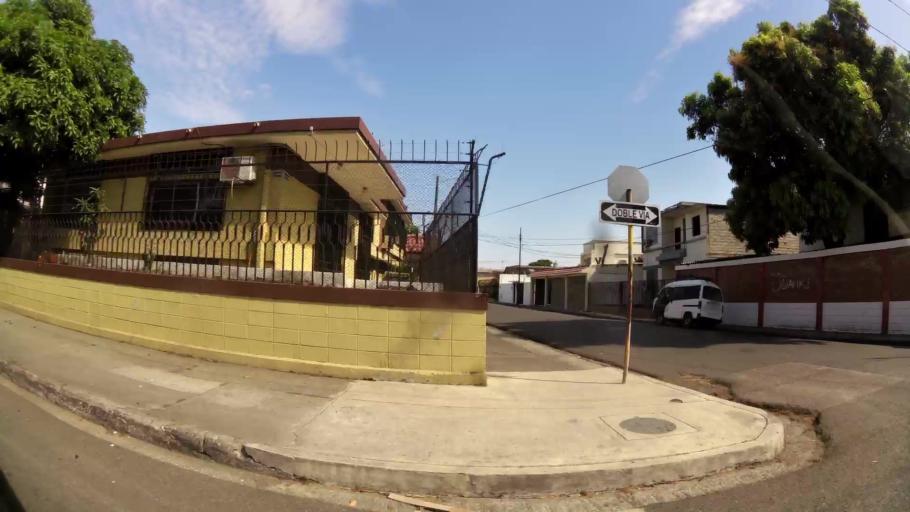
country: EC
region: Guayas
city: Guayaquil
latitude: -2.2203
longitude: -79.8945
